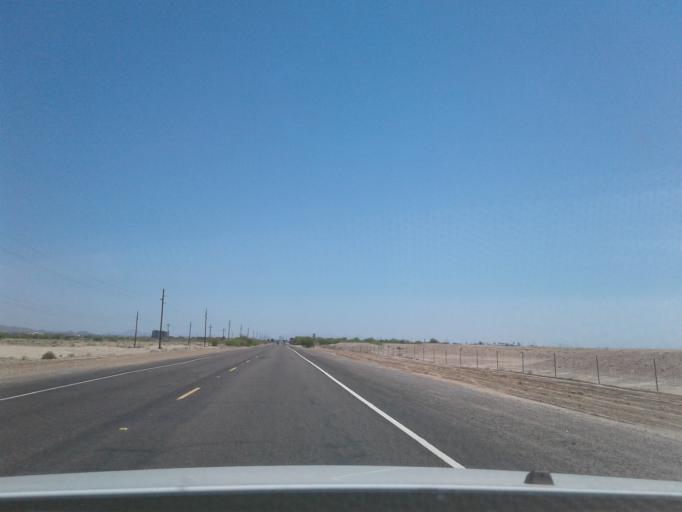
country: US
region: Arizona
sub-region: Maricopa County
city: Sun Lakes
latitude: 33.2522
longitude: -111.9777
